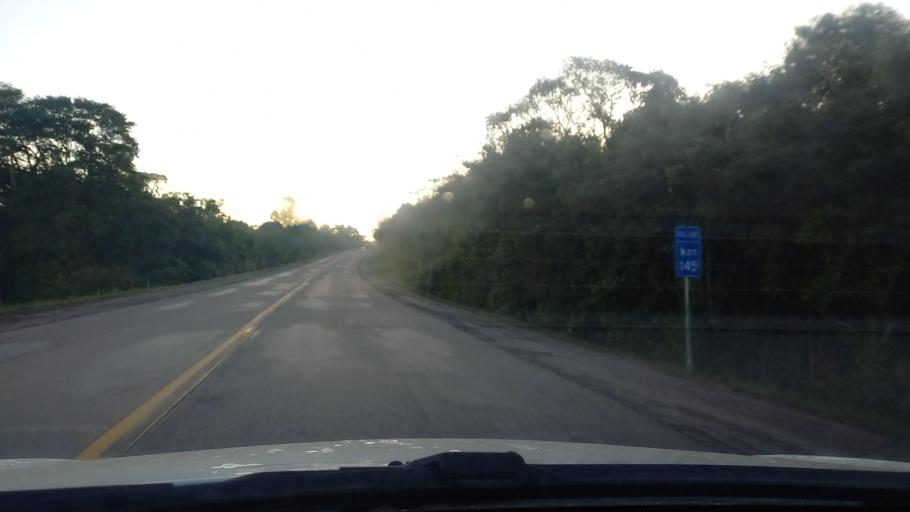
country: BR
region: Rio Grande do Sul
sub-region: Candelaria
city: Candelaria
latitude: -29.6845
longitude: -52.8457
